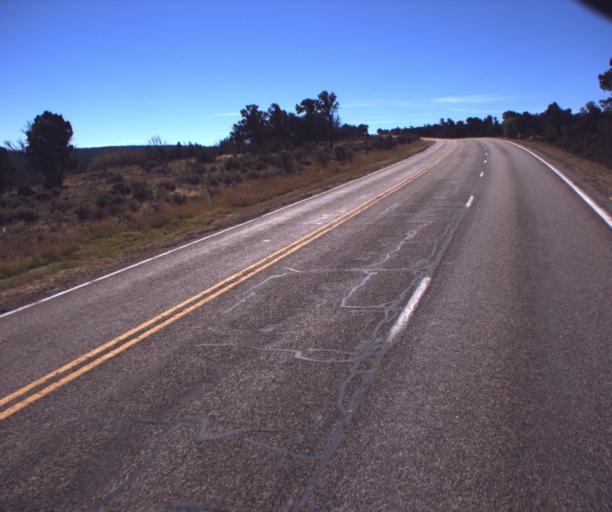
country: US
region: Arizona
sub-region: Coconino County
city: Fredonia
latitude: 36.8079
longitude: -112.2557
